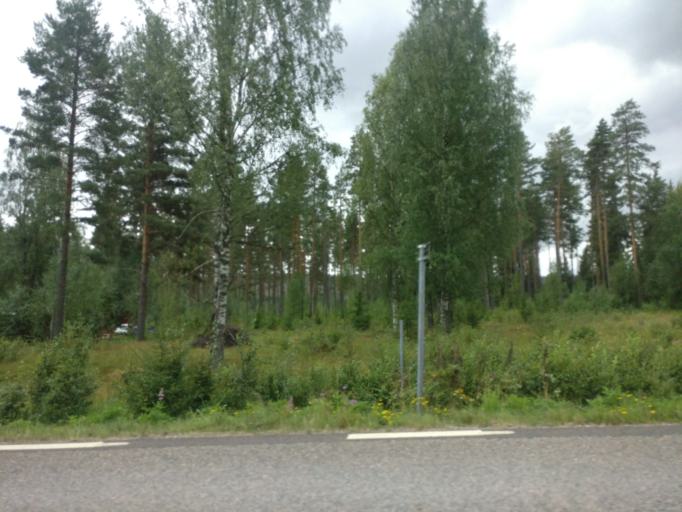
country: SE
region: Vaermland
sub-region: Torsby Kommun
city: Torsby
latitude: 60.7586
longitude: 12.7684
